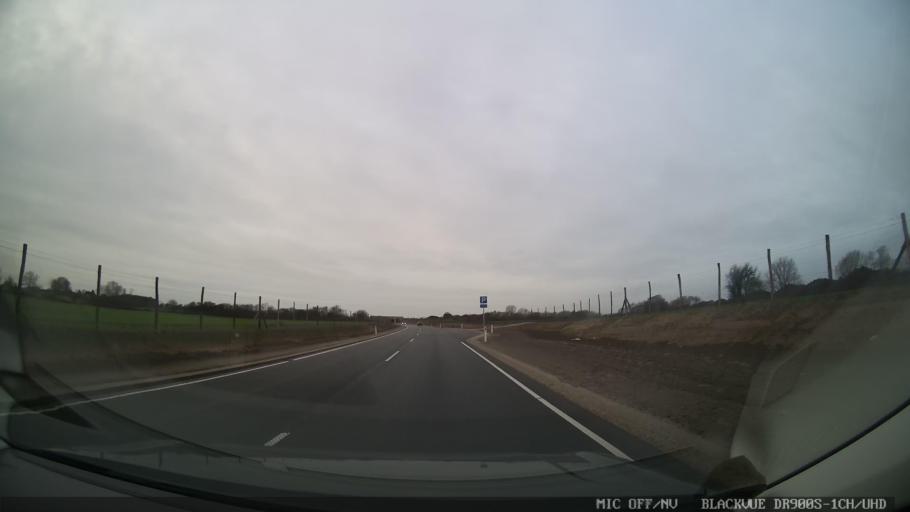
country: DK
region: Central Jutland
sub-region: Arhus Kommune
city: Malling
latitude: 56.0542
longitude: 10.1838
